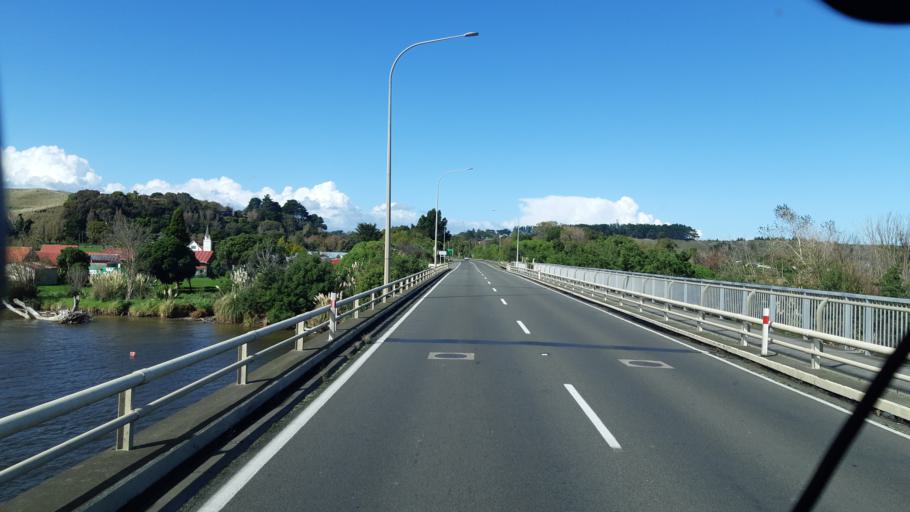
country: NZ
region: Manawatu-Wanganui
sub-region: Wanganui District
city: Wanganui
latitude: -39.9455
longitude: 175.0467
